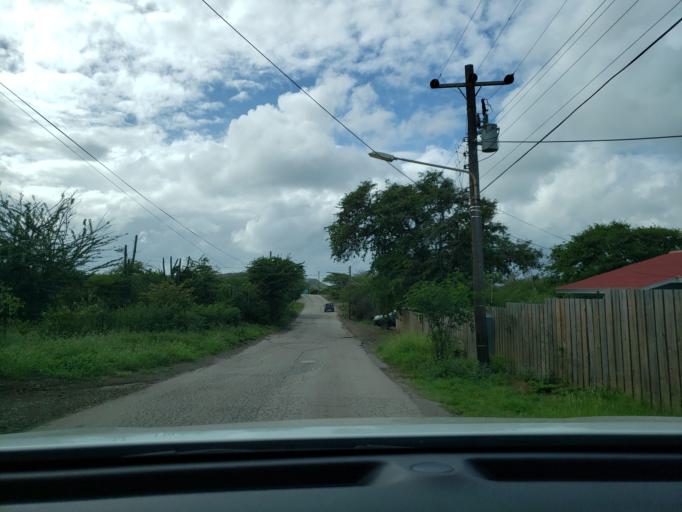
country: CW
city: Dorp Soto
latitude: 12.2171
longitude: -69.0690
